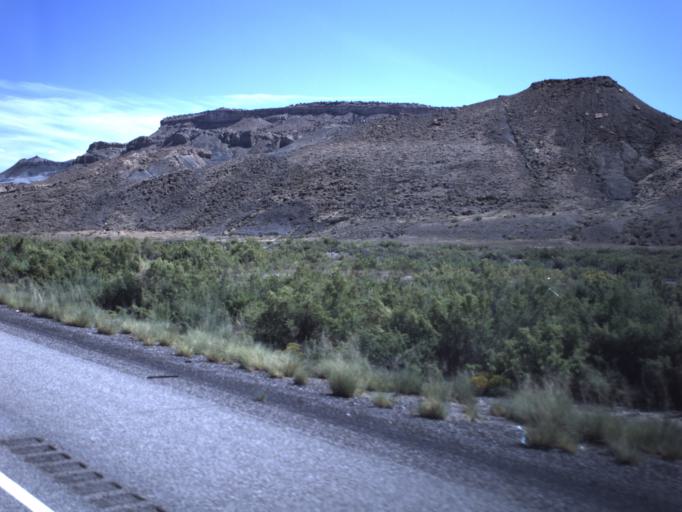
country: US
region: Utah
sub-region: Emery County
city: Ferron
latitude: 38.8098
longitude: -111.2429
